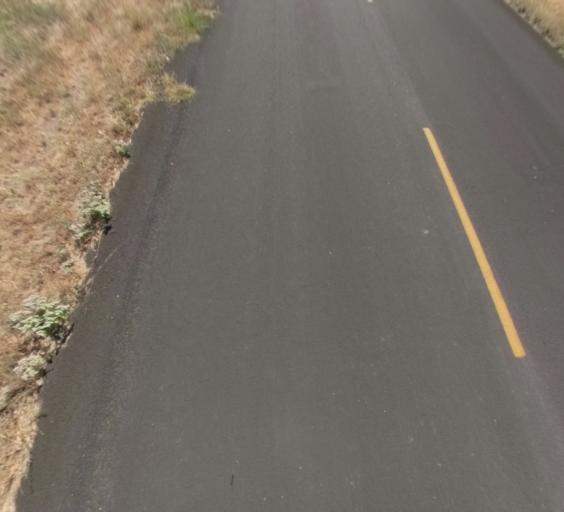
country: US
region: California
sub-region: Madera County
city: Bonadelle Ranchos-Madera Ranchos
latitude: 37.0058
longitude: -119.8891
